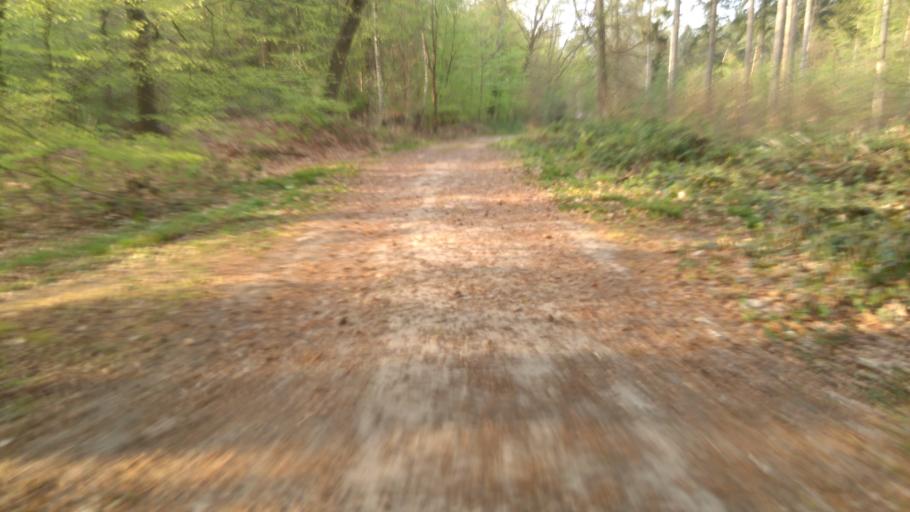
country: DE
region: Lower Saxony
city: Buxtehude
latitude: 53.4699
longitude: 9.6590
